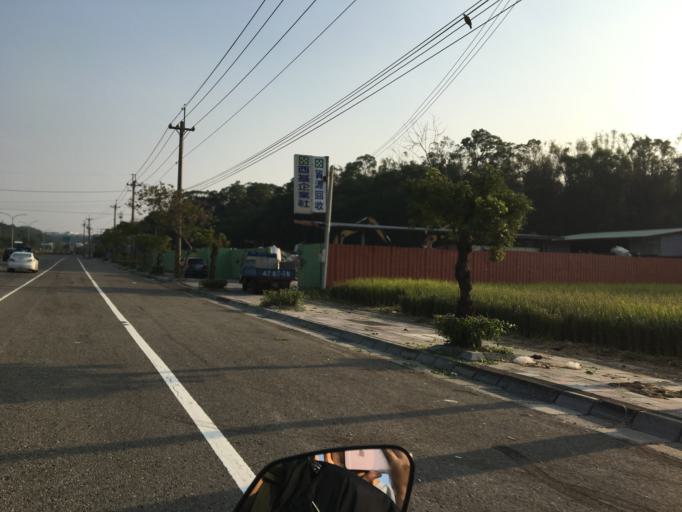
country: TW
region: Taiwan
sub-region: Hsinchu
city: Hsinchu
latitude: 24.7267
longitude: 120.9180
